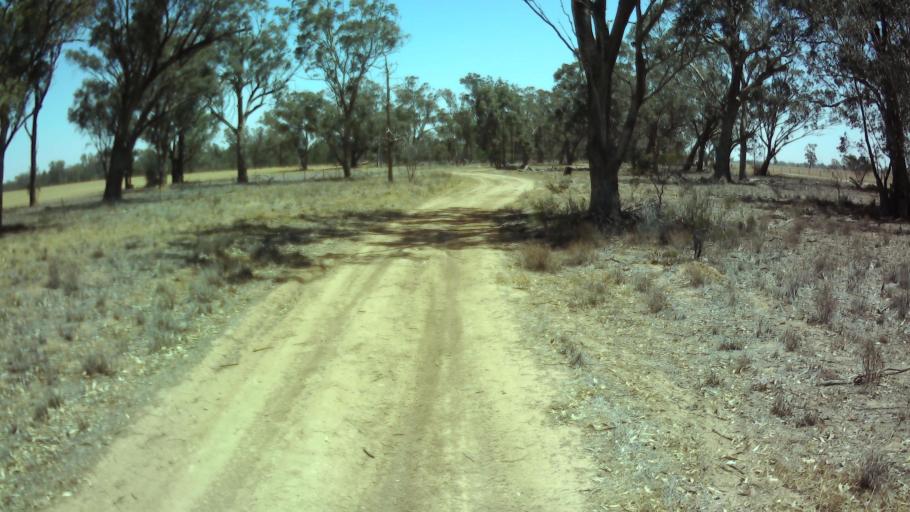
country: AU
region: New South Wales
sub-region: Weddin
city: Grenfell
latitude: -34.0586
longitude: 147.8154
